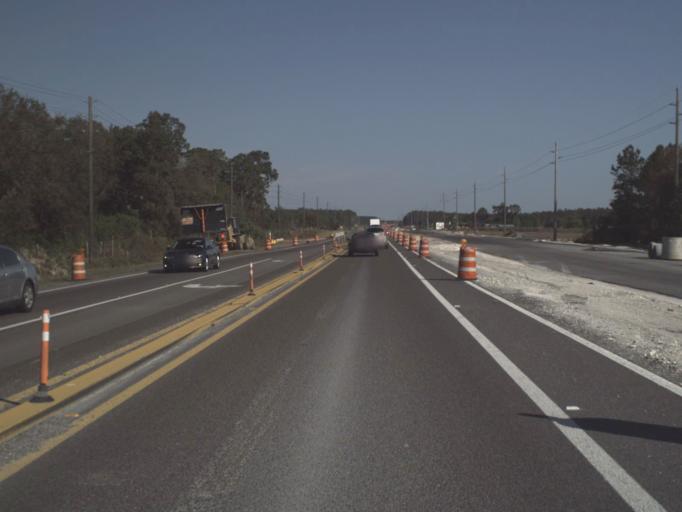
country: US
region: Florida
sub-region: Lake County
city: Four Corners
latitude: 28.4138
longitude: -81.7025
